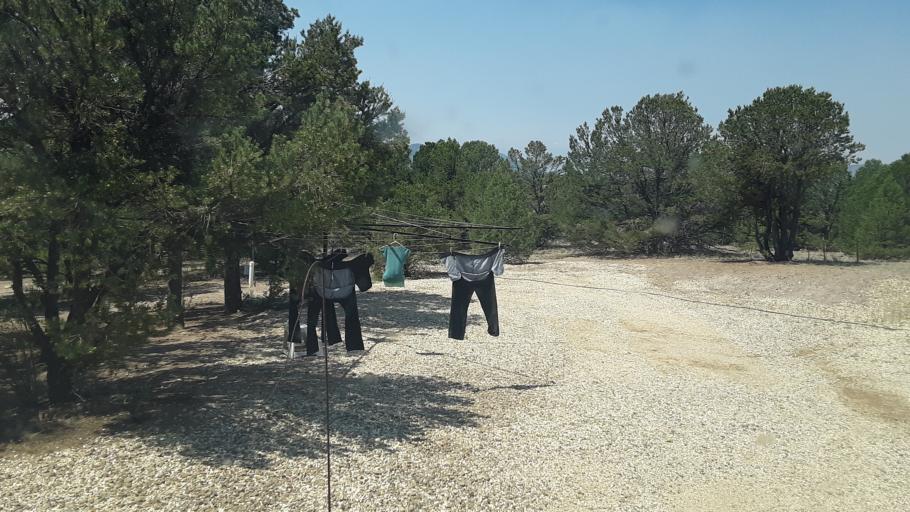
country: US
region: Colorado
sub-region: Custer County
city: Westcliffe
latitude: 38.2908
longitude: -105.4887
